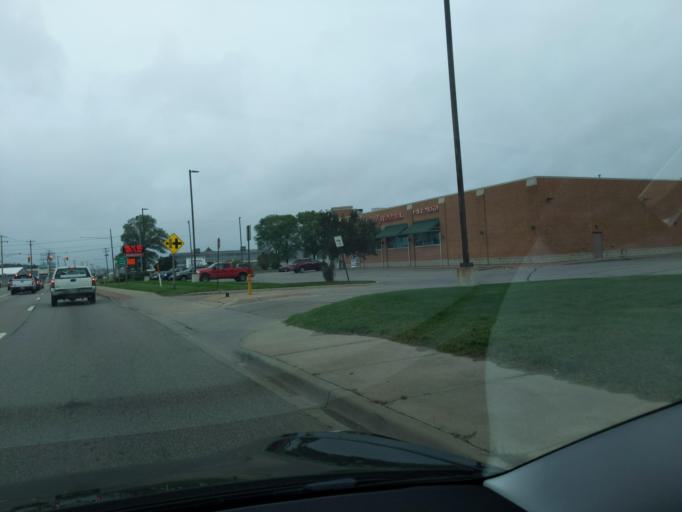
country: US
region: Michigan
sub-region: Wexford County
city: Cadillac
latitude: 44.2659
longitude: -85.4062
